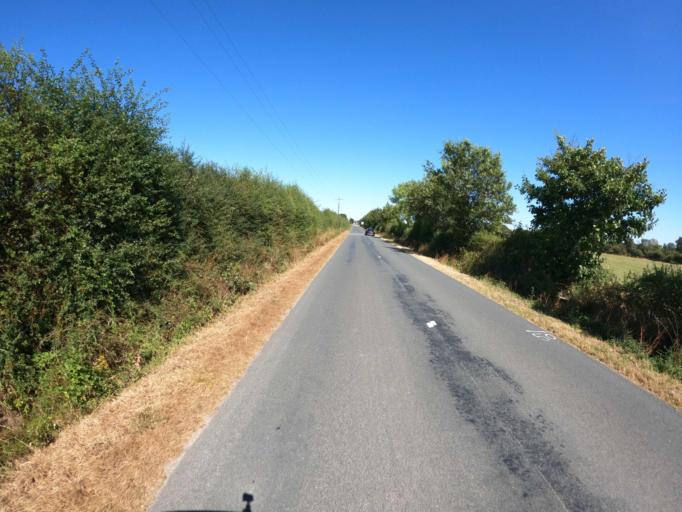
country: FR
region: Pays de la Loire
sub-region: Departement de la Vendee
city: Les Landes-Genusson
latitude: 46.9609
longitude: -1.1325
